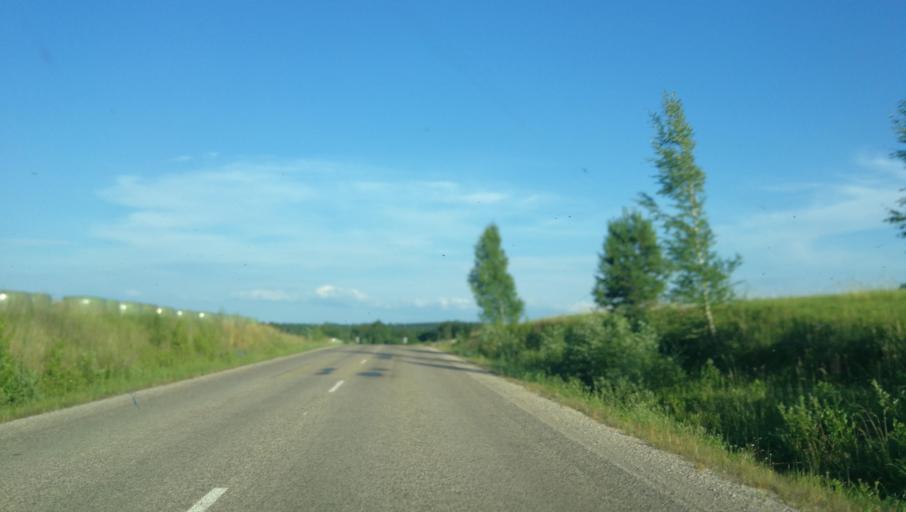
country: LV
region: Priekuli
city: Priekuli
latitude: 57.2700
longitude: 25.3410
